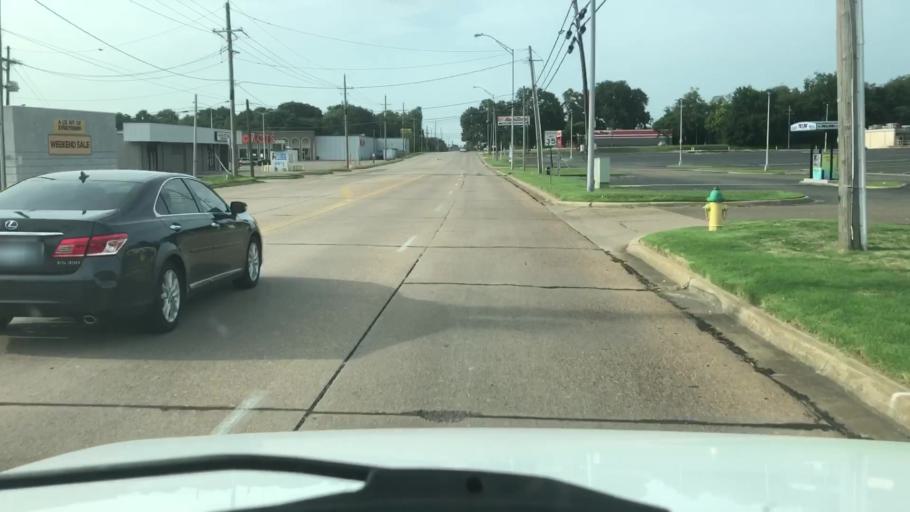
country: US
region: Texas
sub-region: Bowie County
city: Wake Village
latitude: 33.4358
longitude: -94.0805
